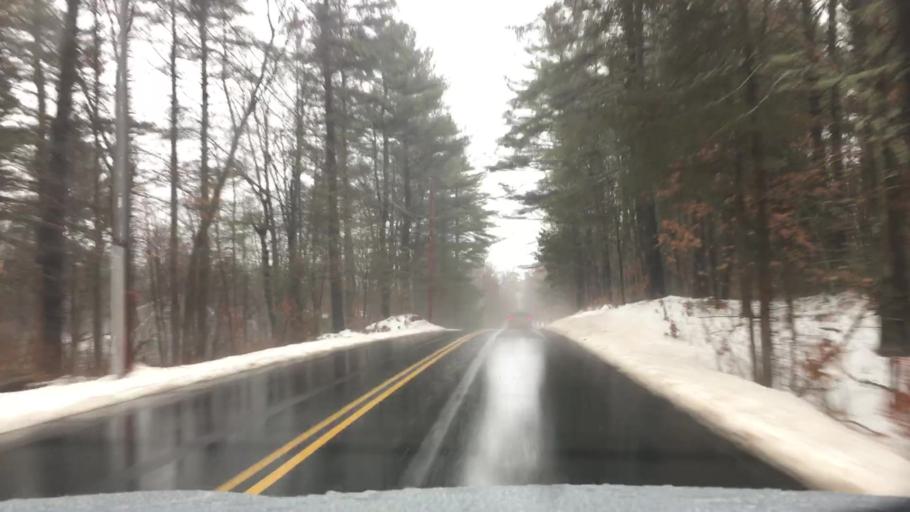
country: US
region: Massachusetts
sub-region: Hampshire County
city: Granby
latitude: 42.2613
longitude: -72.4611
